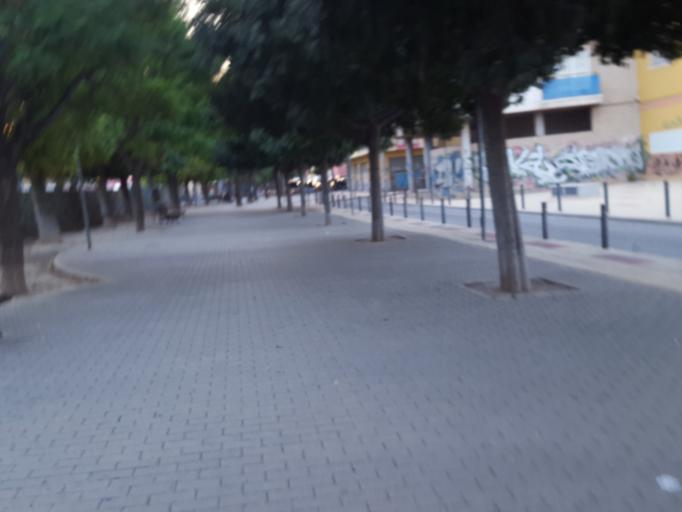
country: ES
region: Murcia
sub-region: Murcia
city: Murcia
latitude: 37.9752
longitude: -1.1351
